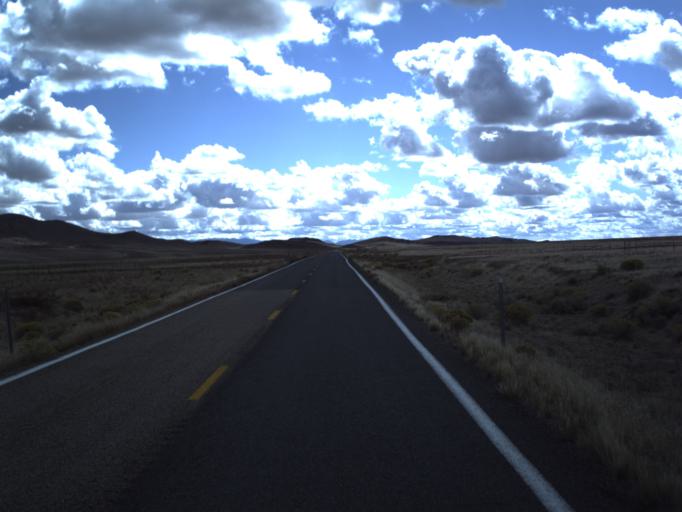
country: US
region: Utah
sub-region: Beaver County
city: Milford
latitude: 38.6593
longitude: -113.8760
